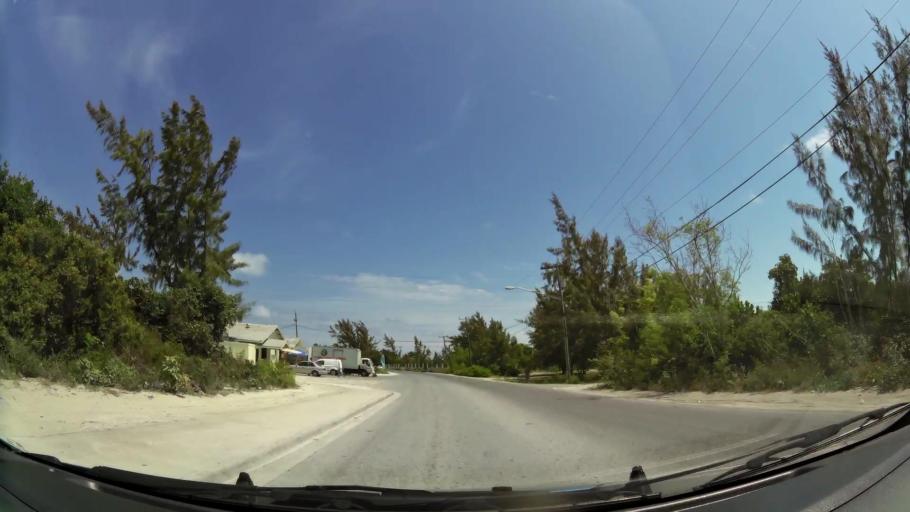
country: BS
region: Mayaguana
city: Abraham's Bay
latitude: 21.7617
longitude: -72.2623
